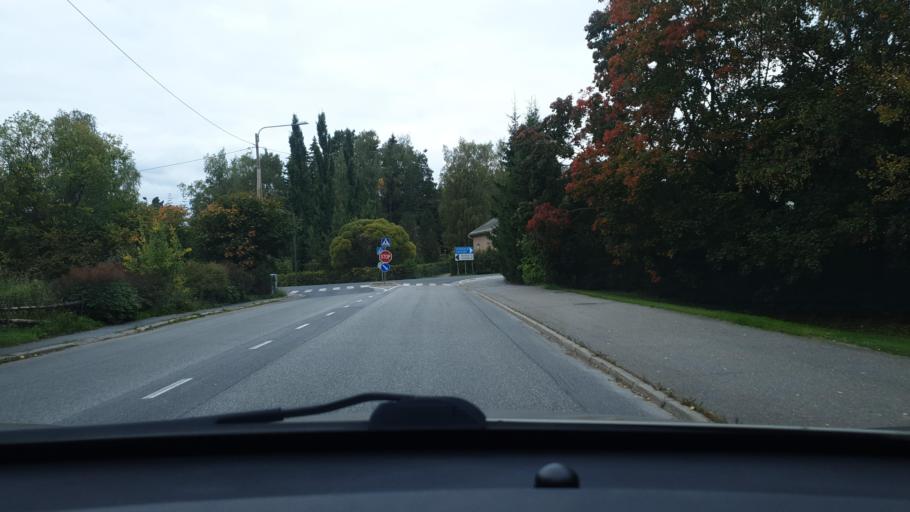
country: FI
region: Ostrobothnia
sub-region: Vaasa
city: Korsholm
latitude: 63.0989
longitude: 21.6684
